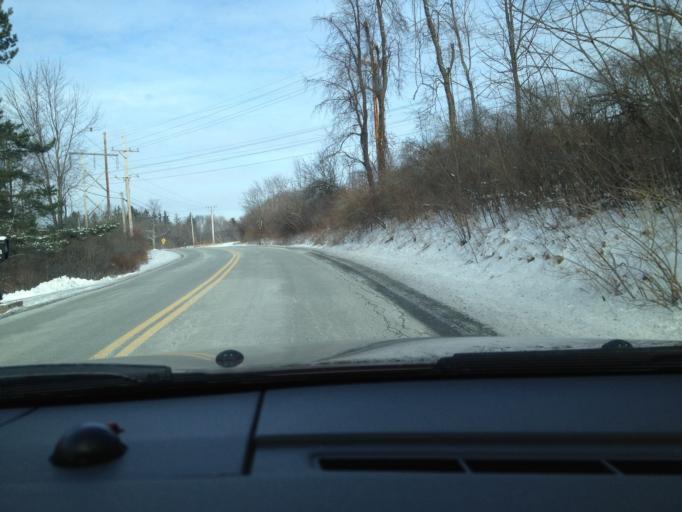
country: US
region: New York
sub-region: Rensselaer County
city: West Sand Lake
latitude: 42.6267
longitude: -73.5941
